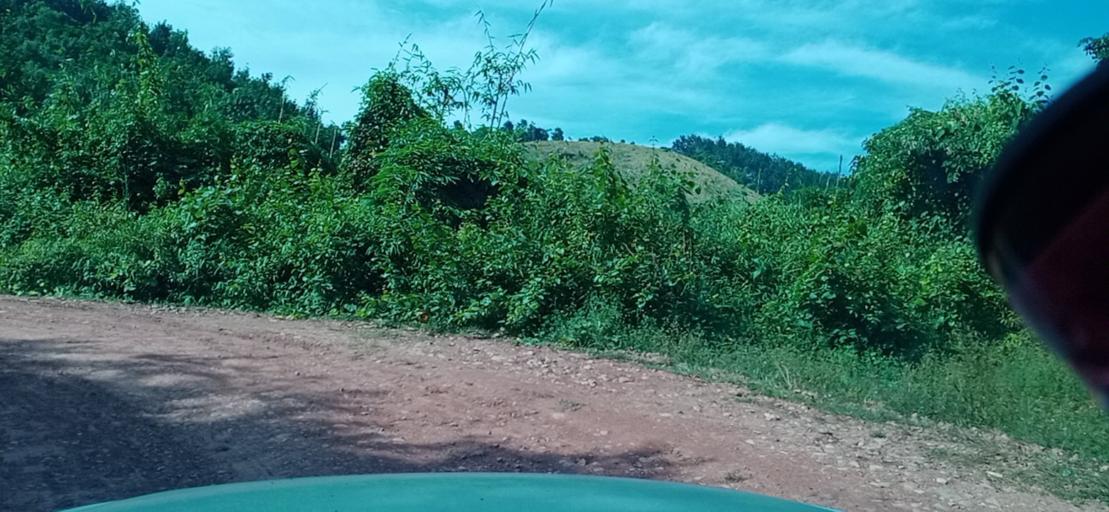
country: TH
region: Changwat Bueng Kan
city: Pak Khat
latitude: 18.6670
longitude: 103.1993
